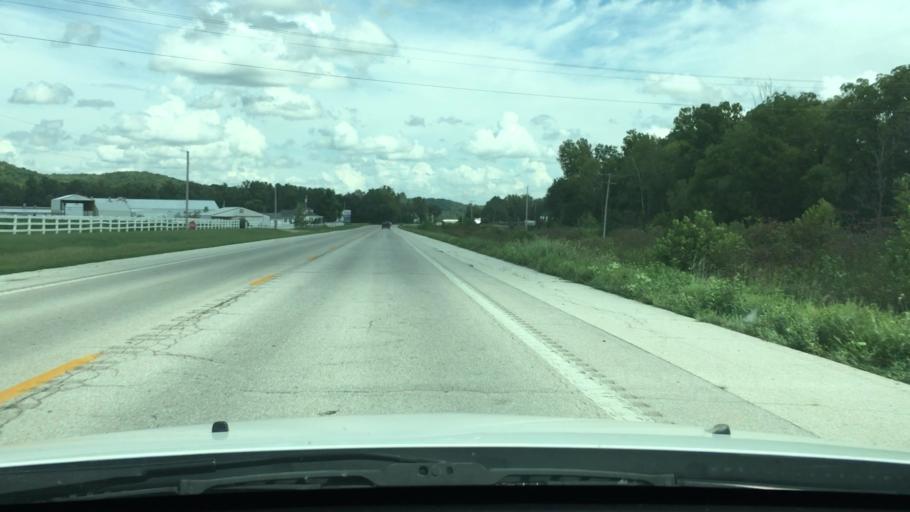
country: US
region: Missouri
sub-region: Pike County
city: Louisiana
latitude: 39.4064
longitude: -91.1055
